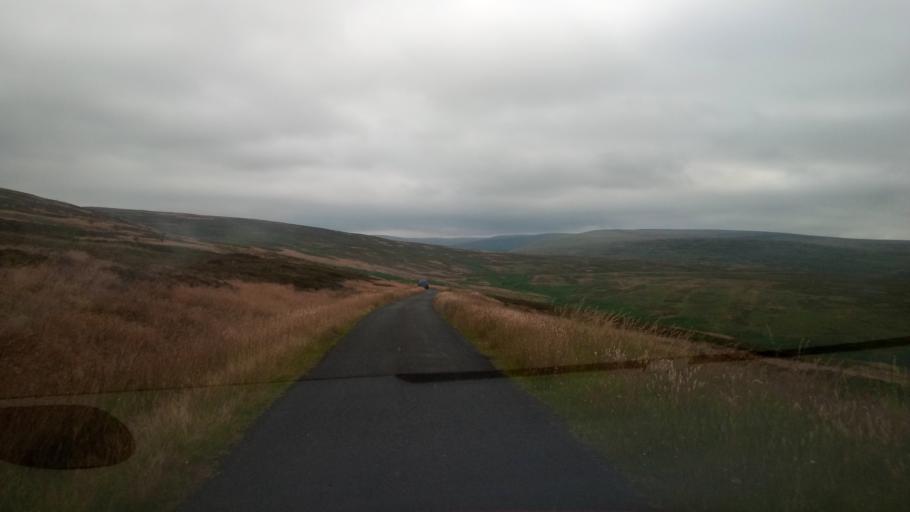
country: GB
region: Scotland
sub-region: Dumfries and Galloway
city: Langholm
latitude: 55.1625
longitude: -2.9640
